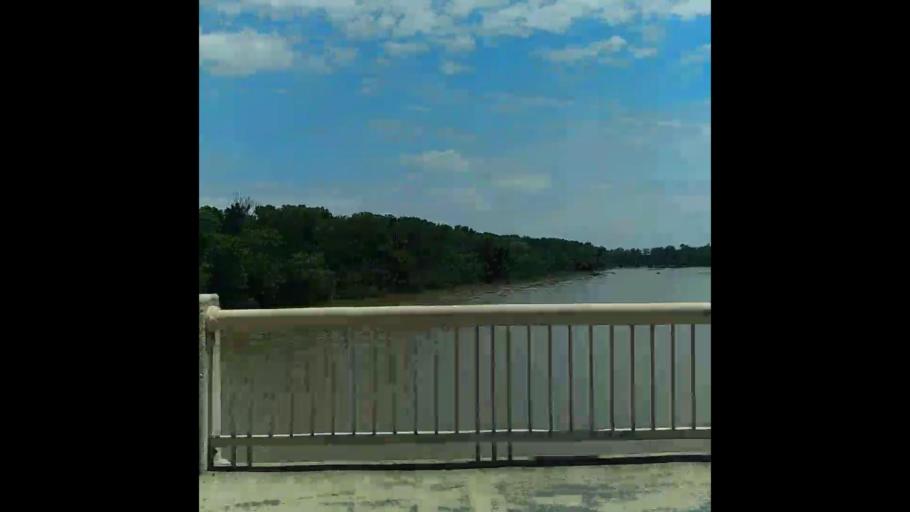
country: US
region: South Carolina
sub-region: Richland County
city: Columbia
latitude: 33.9879
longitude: -81.0469
